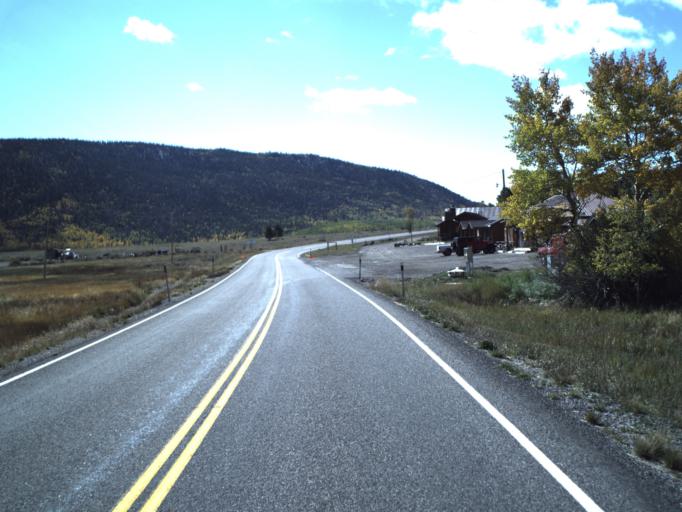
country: US
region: Utah
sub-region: Wayne County
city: Loa
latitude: 38.5362
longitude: -111.7379
